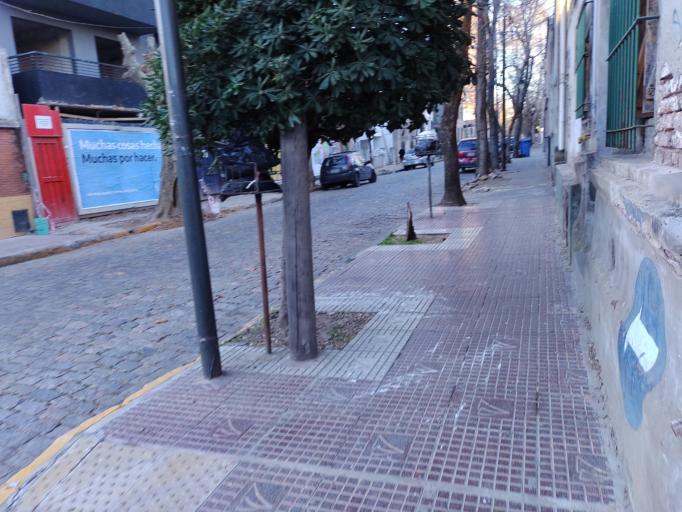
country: AR
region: Buenos Aires
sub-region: Partido de Tigre
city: Tigre
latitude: -34.4401
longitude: -58.5626
